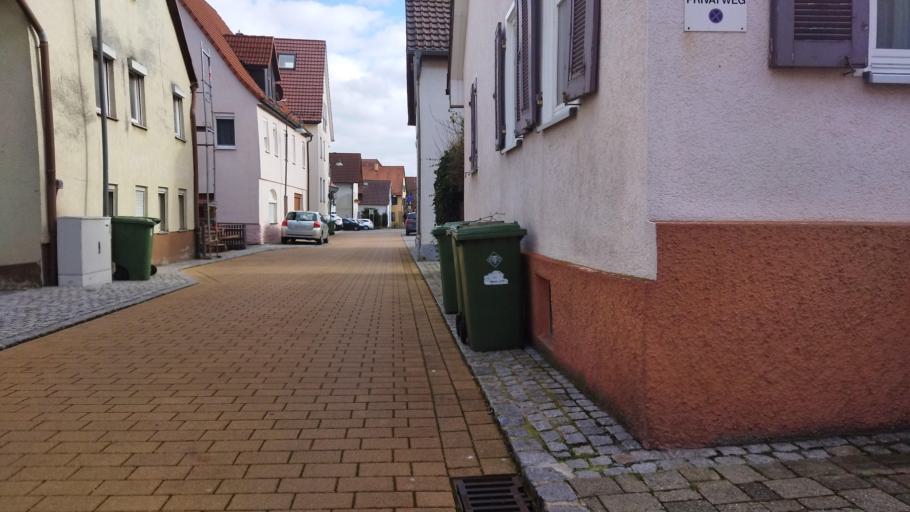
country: DE
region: Baden-Wuerttemberg
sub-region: Regierungsbezirk Stuttgart
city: Freudental
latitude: 49.0100
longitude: 9.0593
